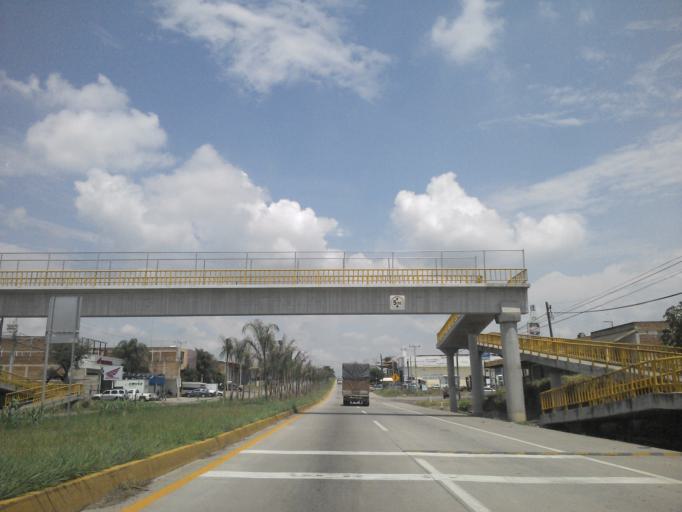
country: MX
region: Jalisco
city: Zapotlanejo
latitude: 20.6093
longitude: -103.0873
